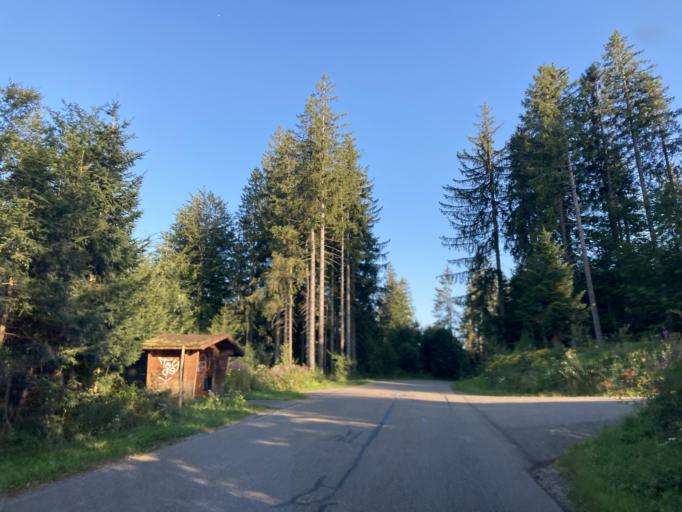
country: DE
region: Baden-Wuerttemberg
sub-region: Freiburg Region
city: Schonach im Schwarzwald
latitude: 48.1655
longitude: 8.1865
